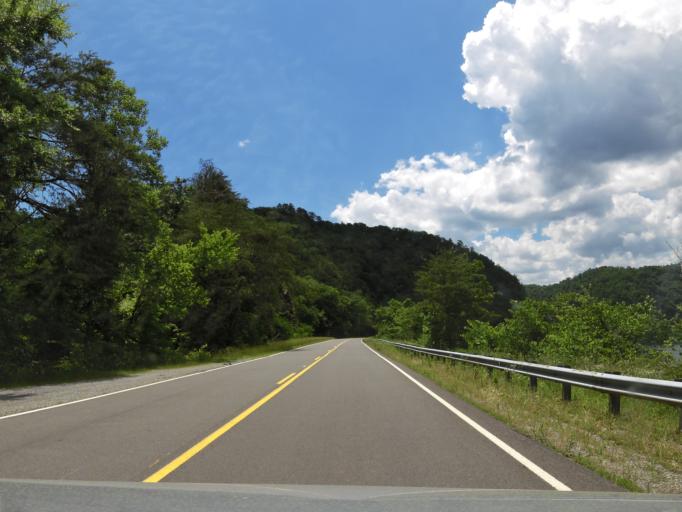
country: US
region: Tennessee
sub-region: Loudon County
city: Greenback
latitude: 35.5329
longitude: -83.9918
